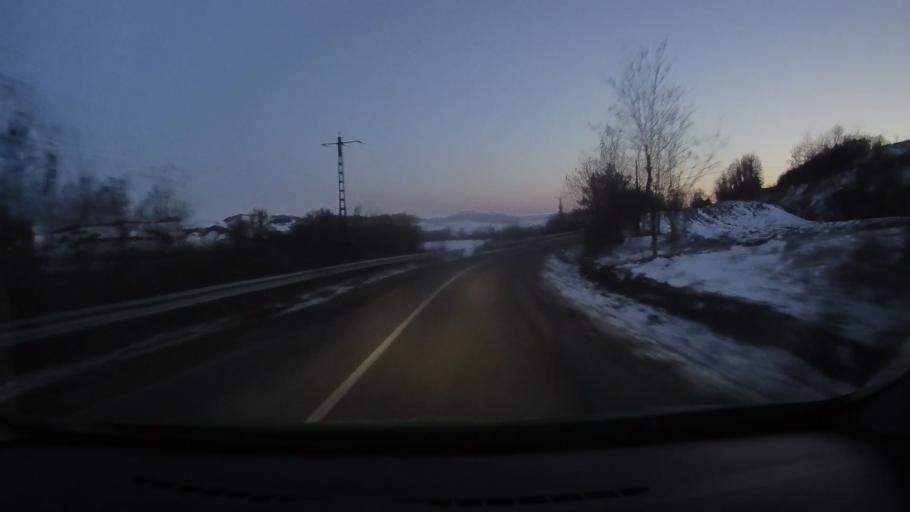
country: RO
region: Sibiu
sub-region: Comuna Brateiu
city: Brateiu
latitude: 46.1956
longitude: 24.4433
